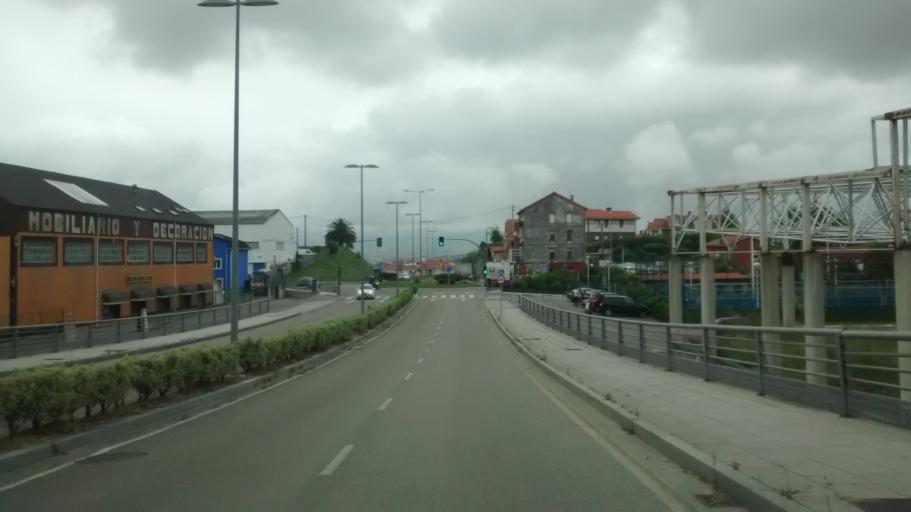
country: ES
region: Cantabria
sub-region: Provincia de Cantabria
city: Santa Cruz de Bezana
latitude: 43.4485
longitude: -3.8673
